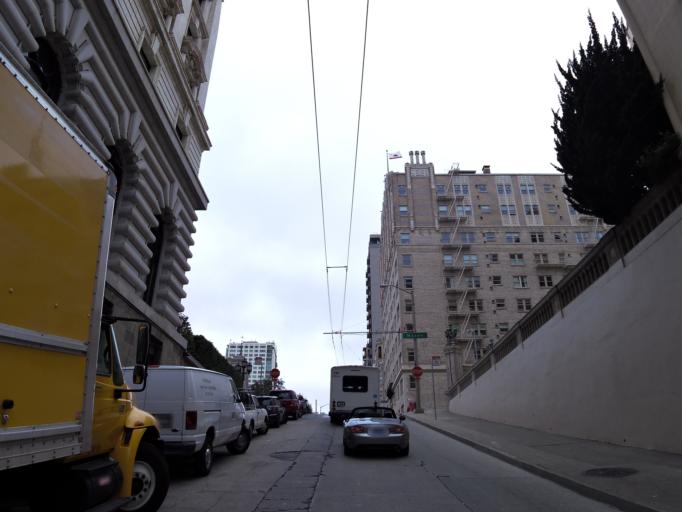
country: US
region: California
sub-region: San Francisco County
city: San Francisco
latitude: 37.7928
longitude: -122.4105
